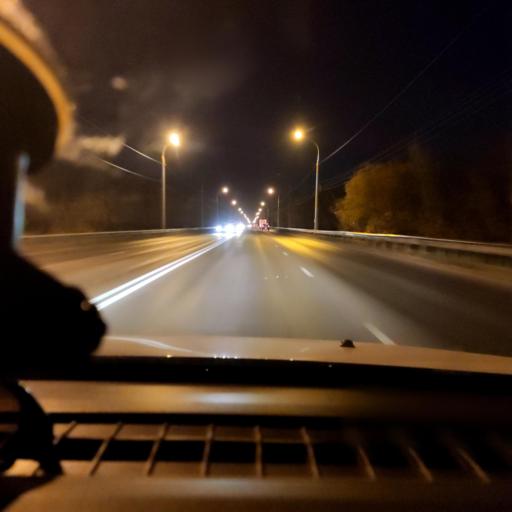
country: RU
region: Samara
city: Samara
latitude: 53.1494
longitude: 50.1855
